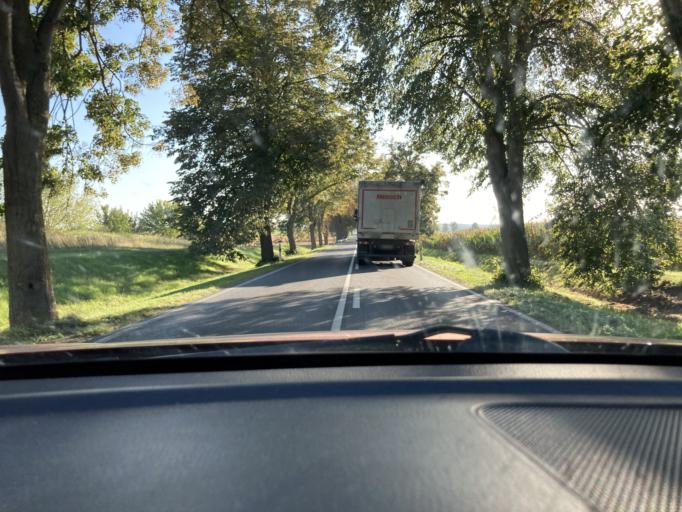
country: DE
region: Mecklenburg-Vorpommern
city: Alt-Sanitz
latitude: 53.7701
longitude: 13.6501
